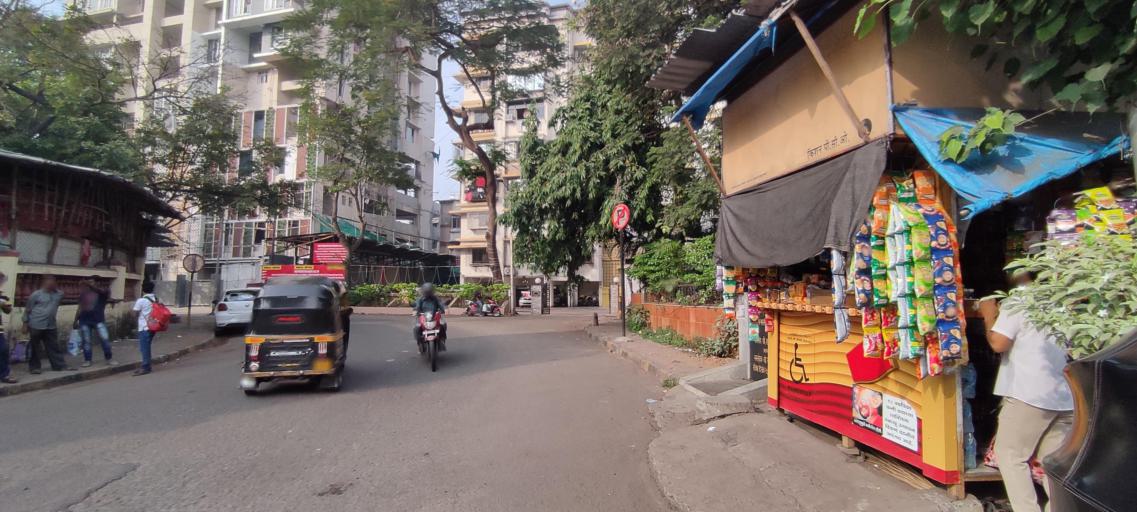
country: IN
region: Maharashtra
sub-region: Mumbai Suburban
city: Mumbai
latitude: 19.0565
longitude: 72.8367
